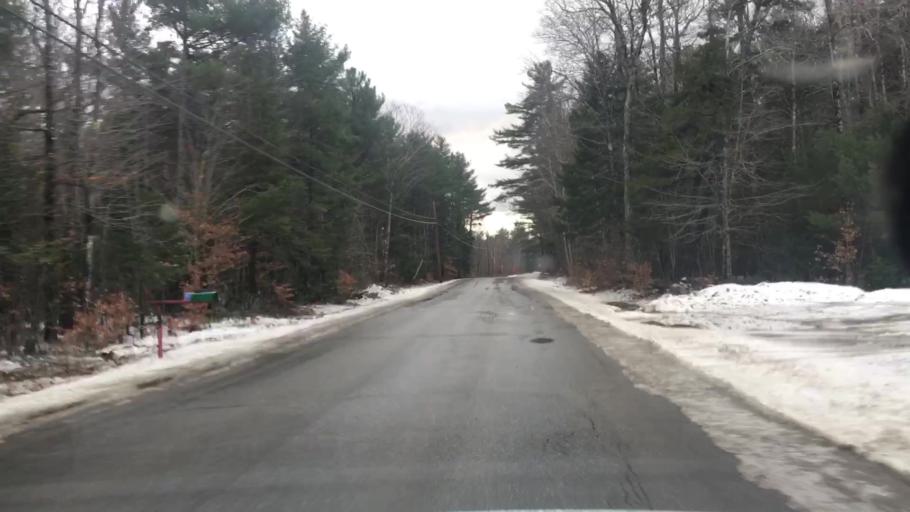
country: US
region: Maine
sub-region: Hancock County
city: Dedham
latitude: 44.6490
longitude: -68.7043
